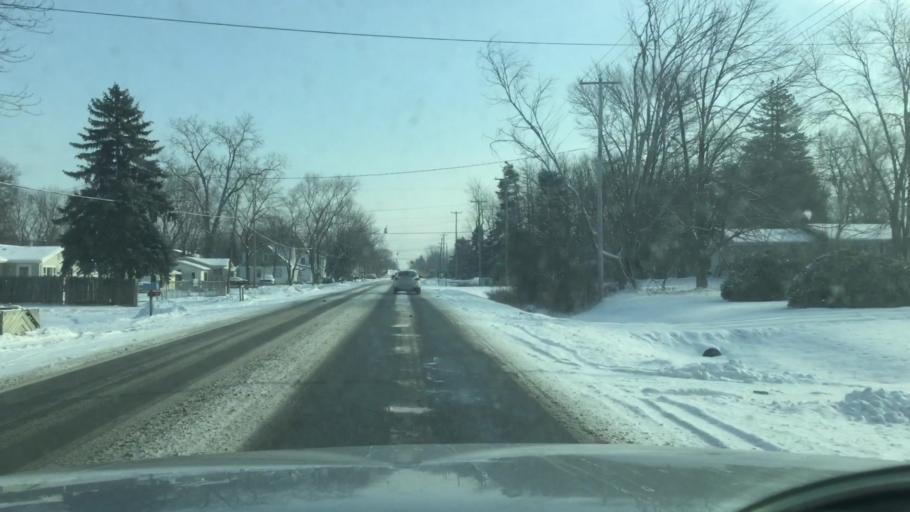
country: US
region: Michigan
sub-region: Genesee County
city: Mount Morris
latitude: 43.1048
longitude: -83.6981
